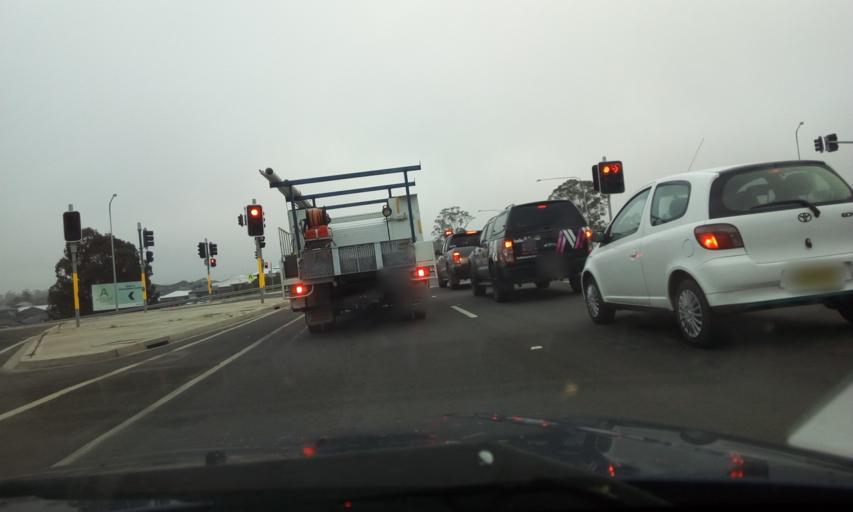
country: AU
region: New South Wales
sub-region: Camden
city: Narellan Vale
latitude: -34.0611
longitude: 150.7269
